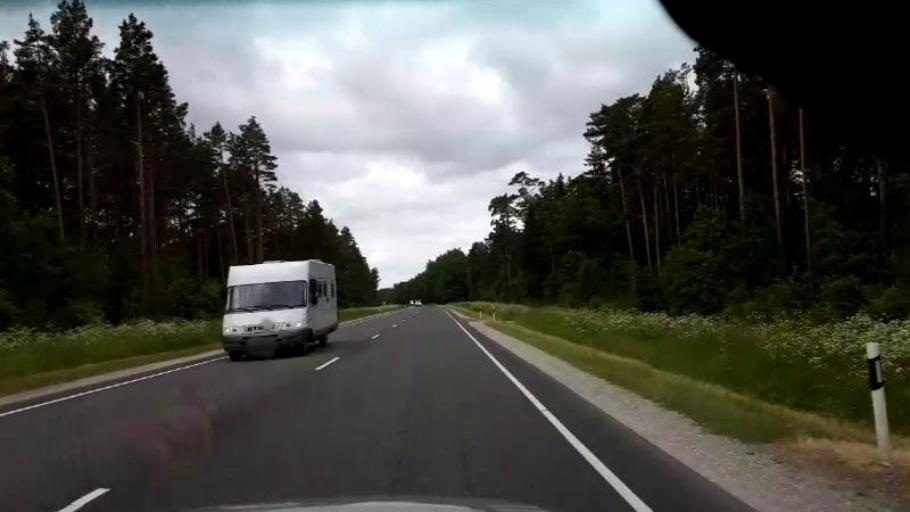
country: EE
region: Paernumaa
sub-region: Paernu linn
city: Parnu
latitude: 58.2724
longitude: 24.5581
